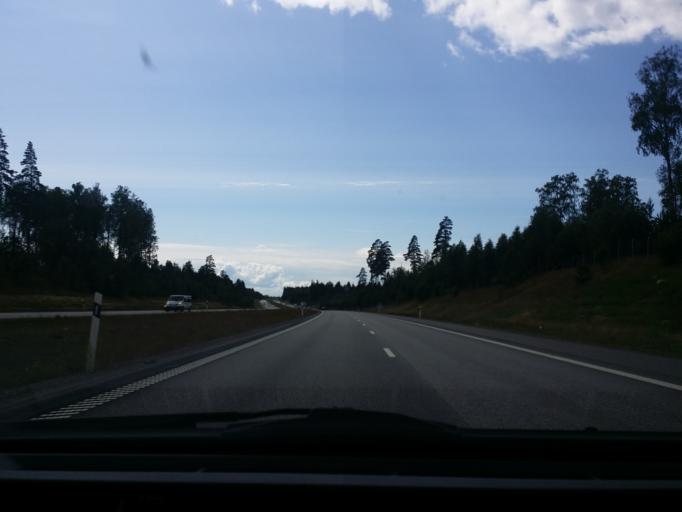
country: SE
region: OErebro
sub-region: Lindesbergs Kommun
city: Fellingsbro
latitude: 59.3675
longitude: 15.5787
